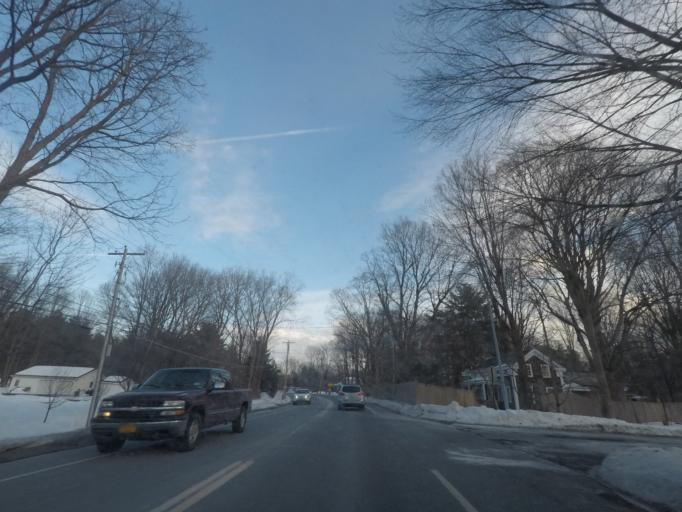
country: US
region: New York
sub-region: Saratoga County
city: Country Knolls
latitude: 42.8391
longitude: -73.7790
